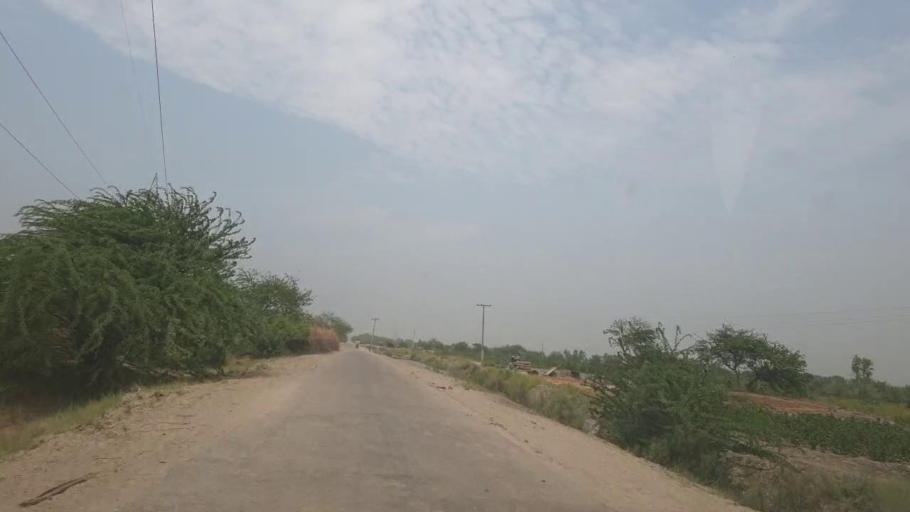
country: PK
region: Sindh
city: Kot Diji
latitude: 27.4346
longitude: 68.7106
